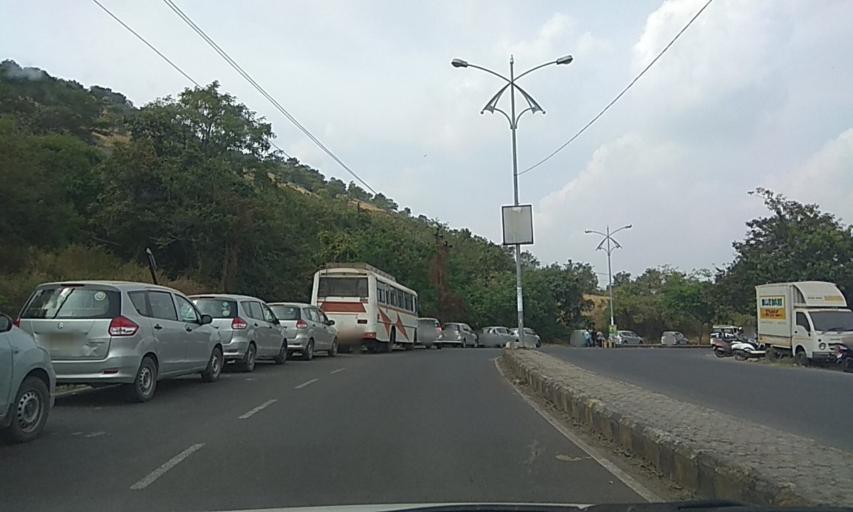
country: IN
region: Maharashtra
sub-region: Pune Division
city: Pimpri
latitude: 18.6003
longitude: 73.7154
